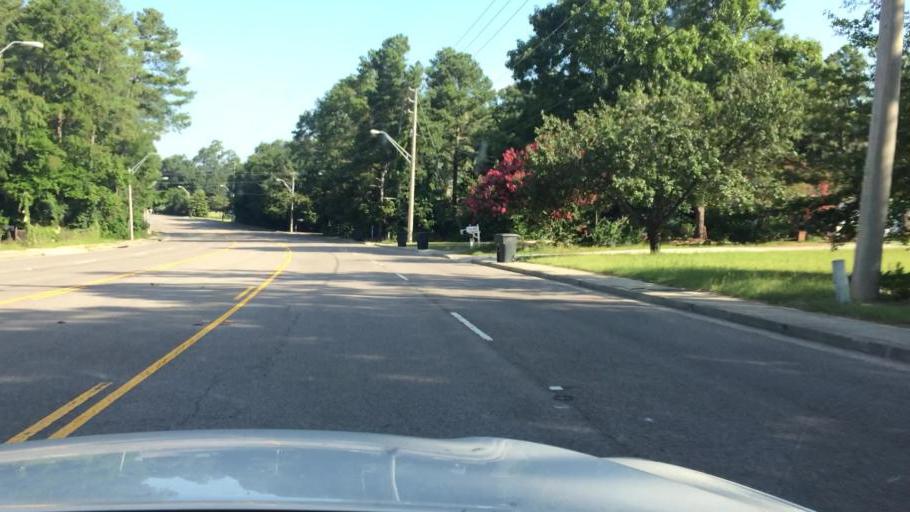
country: US
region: South Carolina
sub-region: Aiken County
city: North Augusta
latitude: 33.5278
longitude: -81.9799
